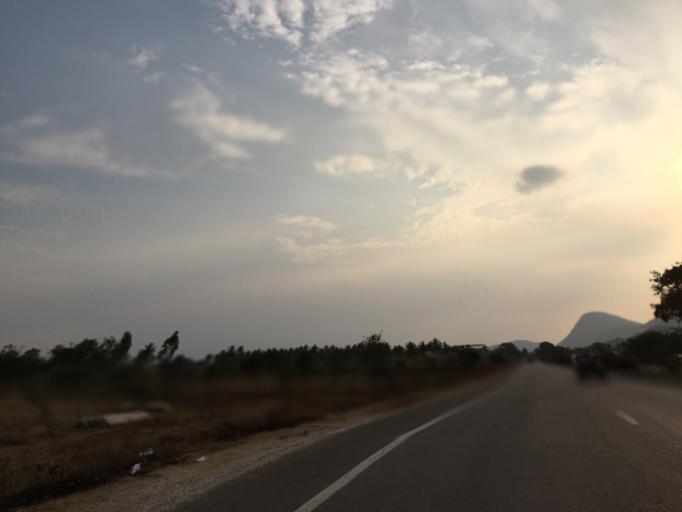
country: IN
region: Karnataka
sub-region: Chikkaballapur
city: Chik Ballapur
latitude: 13.3872
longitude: 77.7325
